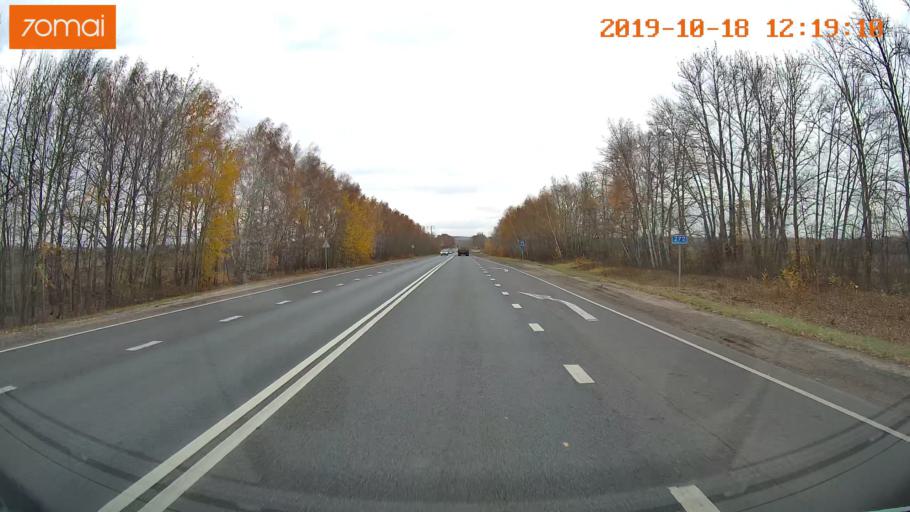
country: RU
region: Rjazan
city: Zakharovo
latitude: 54.4785
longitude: 39.4651
